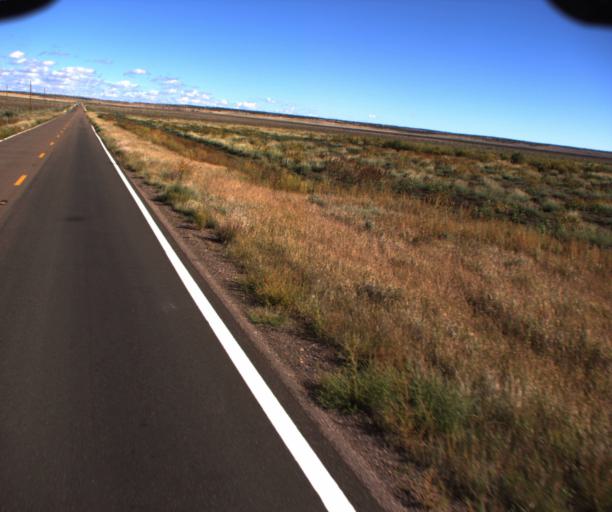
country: US
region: Arizona
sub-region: Apache County
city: Saint Johns
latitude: 34.6157
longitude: -109.3181
